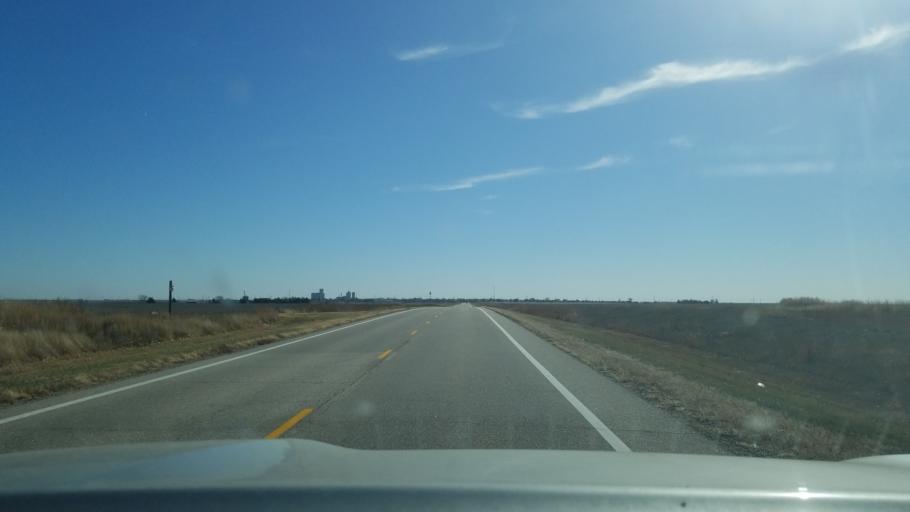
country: US
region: Kansas
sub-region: Kiowa County
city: Greensburg
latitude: 37.5666
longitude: -99.6581
